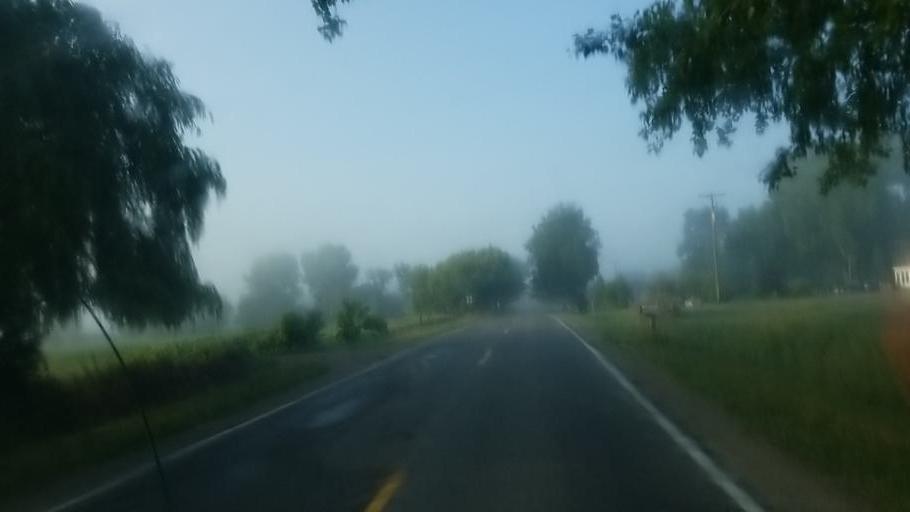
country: US
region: Michigan
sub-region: Muskegon County
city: Twin Lake
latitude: 43.4551
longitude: -86.0791
